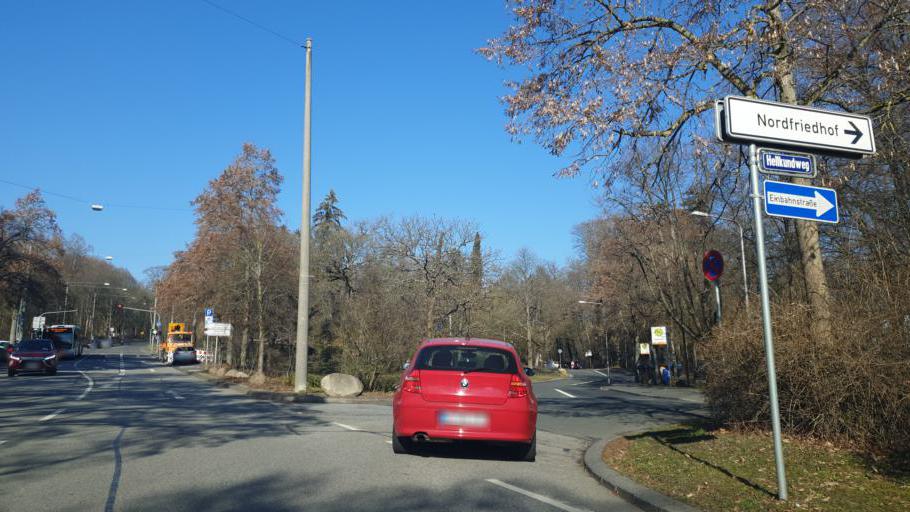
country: DE
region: Hesse
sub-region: Regierungsbezirk Darmstadt
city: Wiesbaden
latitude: 50.0961
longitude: 8.2211
